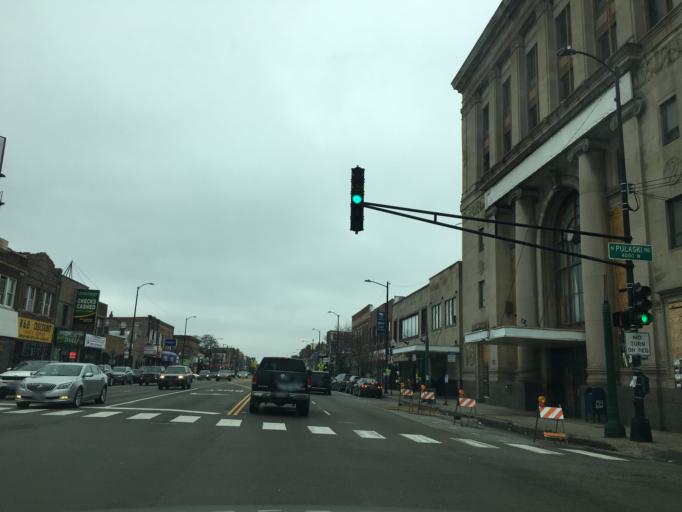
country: US
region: Illinois
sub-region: Cook County
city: Oak Park
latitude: 41.9100
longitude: -87.7263
